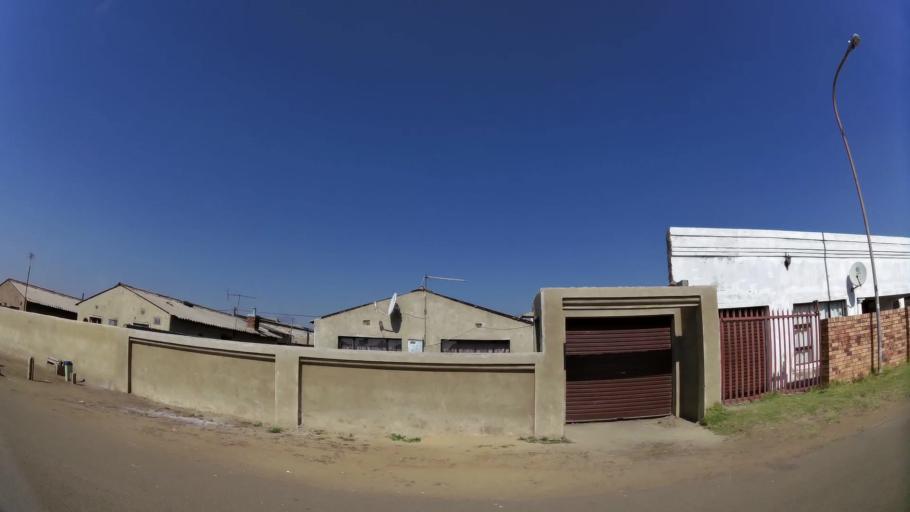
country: ZA
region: Gauteng
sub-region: Ekurhuleni Metropolitan Municipality
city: Benoni
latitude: -26.2205
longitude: 28.3064
